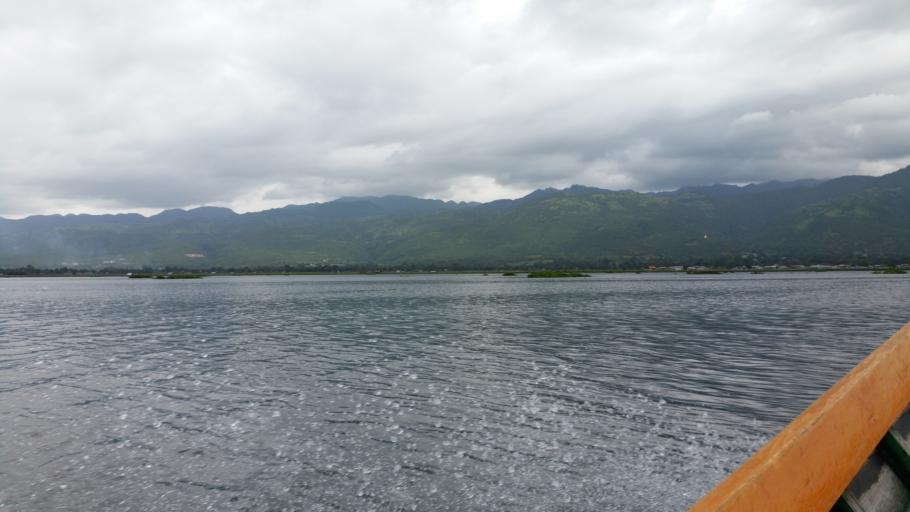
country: MM
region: Shan
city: Taunggyi
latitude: 20.5845
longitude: 96.9215
